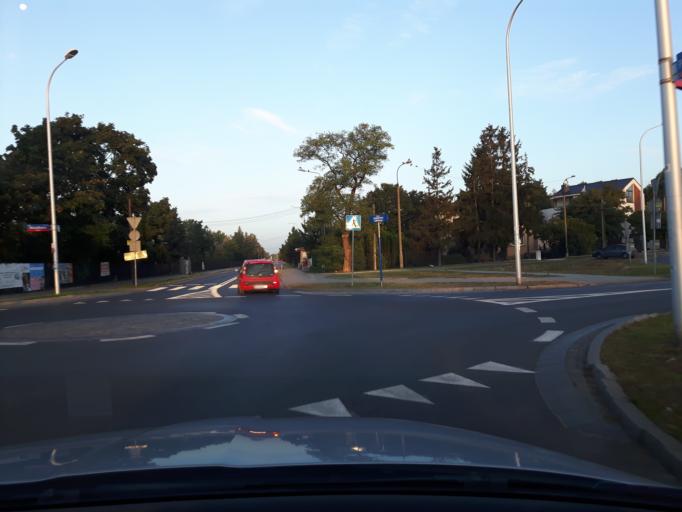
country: PL
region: Masovian Voivodeship
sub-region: Warszawa
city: Wawer
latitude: 52.1843
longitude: 21.1772
